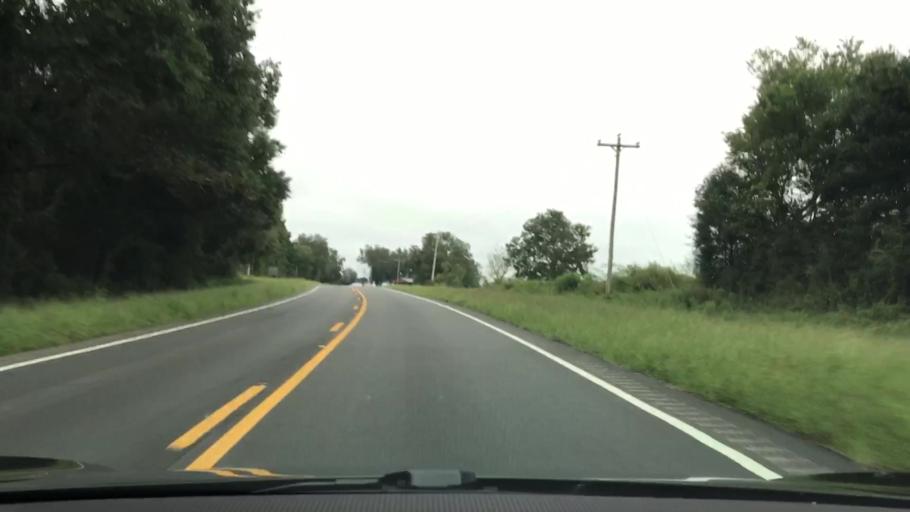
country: US
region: Alabama
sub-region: Covington County
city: Opp
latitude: 31.2313
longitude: -86.1617
